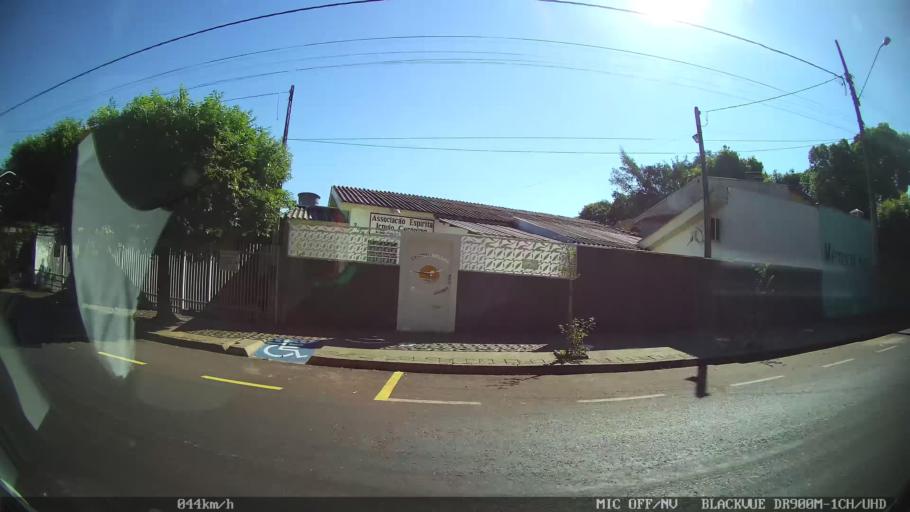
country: BR
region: Sao Paulo
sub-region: Sao Jose Do Rio Preto
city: Sao Jose do Rio Preto
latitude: -20.8120
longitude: -49.4245
